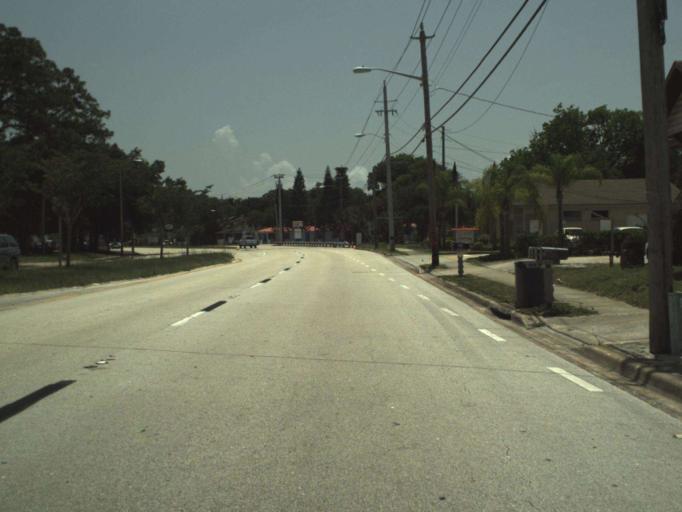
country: US
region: Florida
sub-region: Volusia County
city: Port Orange
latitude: 29.1317
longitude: -80.9825
